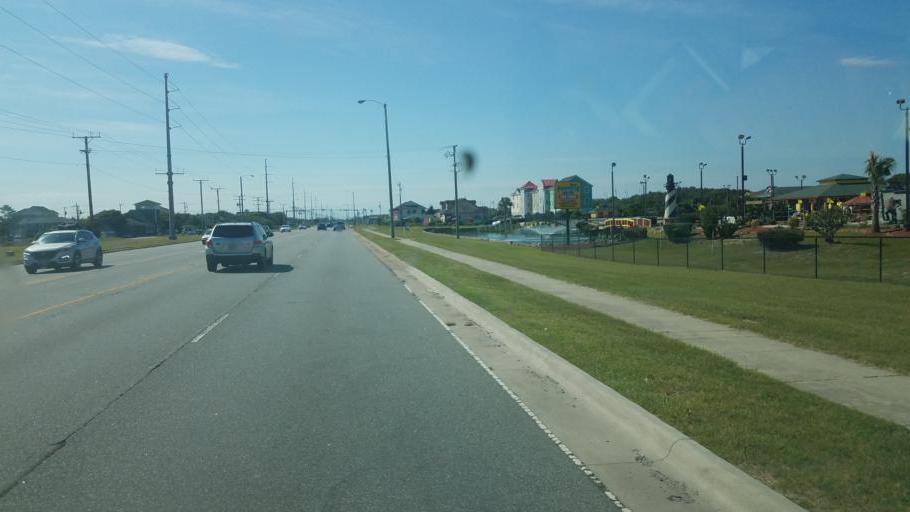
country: US
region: North Carolina
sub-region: Dare County
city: Kitty Hawk
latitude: 36.0539
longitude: -75.6856
